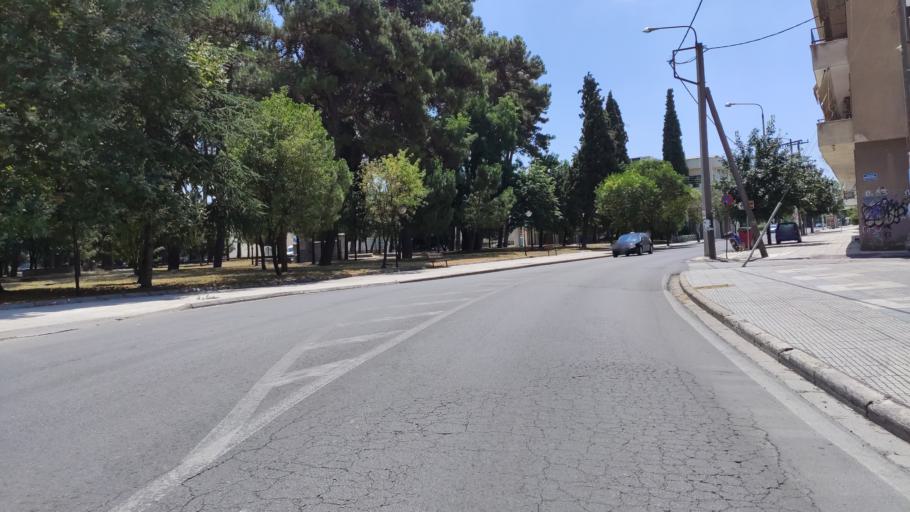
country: GR
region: East Macedonia and Thrace
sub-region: Nomos Rodopis
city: Komotini
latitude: 41.1163
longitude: 25.3983
